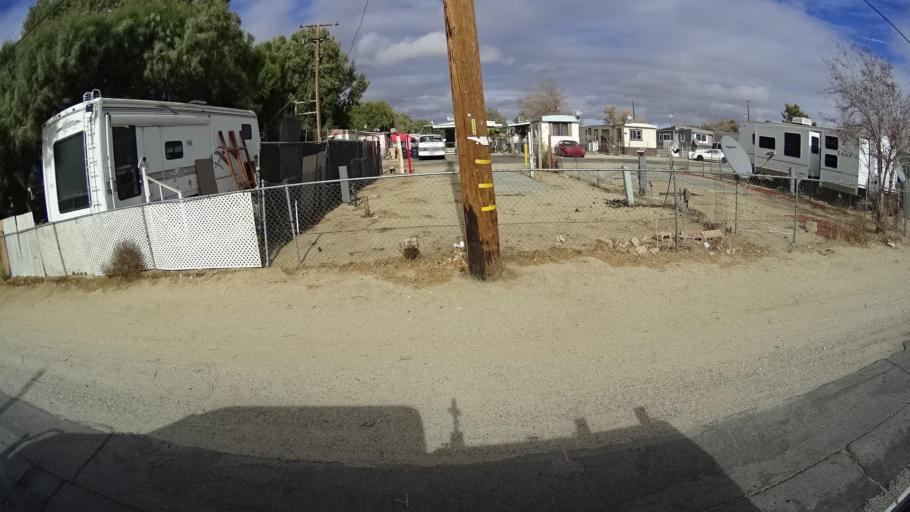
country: US
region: California
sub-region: Kern County
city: Rosamond
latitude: 34.8638
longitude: -118.2252
